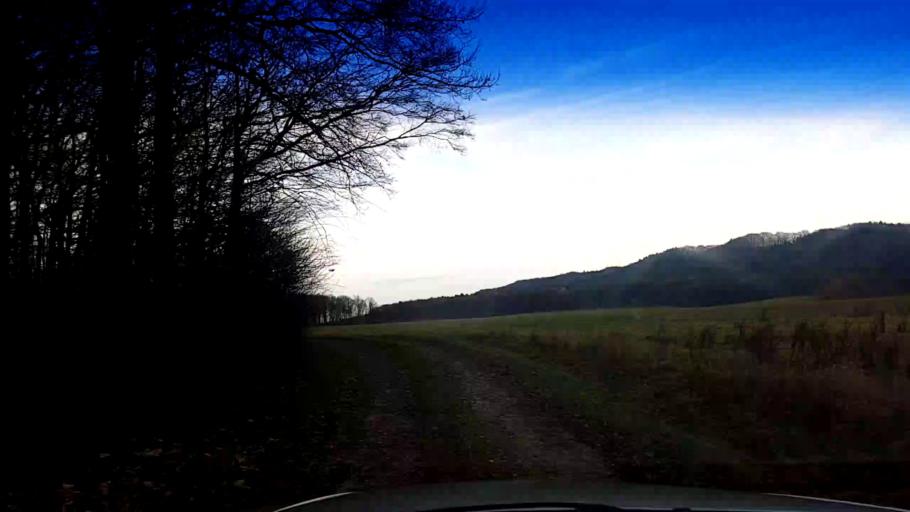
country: DE
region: Bavaria
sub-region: Upper Franconia
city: Schesslitz
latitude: 49.9936
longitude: 11.0304
